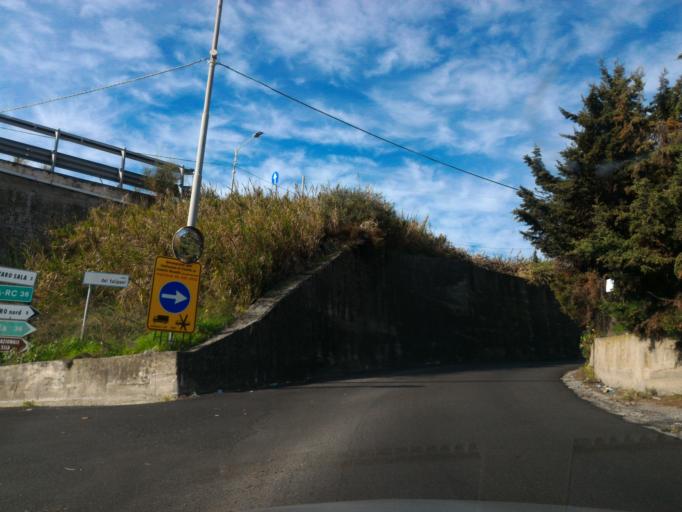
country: IT
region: Calabria
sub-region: Provincia di Catanzaro
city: Cava-Cuculera Nobile
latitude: 38.8991
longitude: 16.6219
